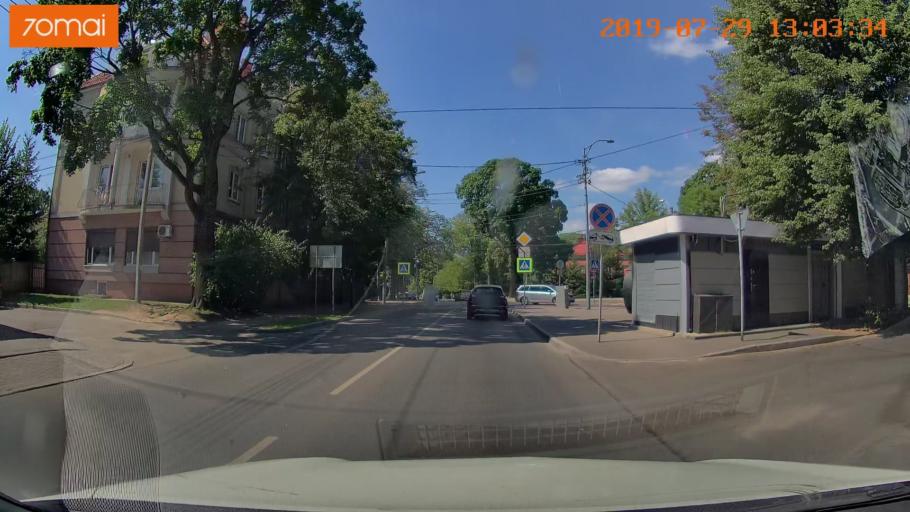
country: RU
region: Kaliningrad
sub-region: Gorod Kaliningrad
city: Kaliningrad
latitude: 54.7151
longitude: 20.4666
